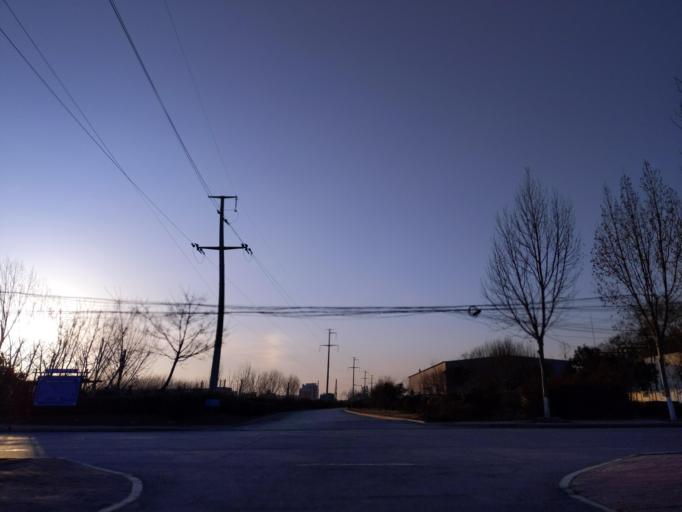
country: CN
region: Henan Sheng
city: Puyang
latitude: 35.7708
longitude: 114.9940
